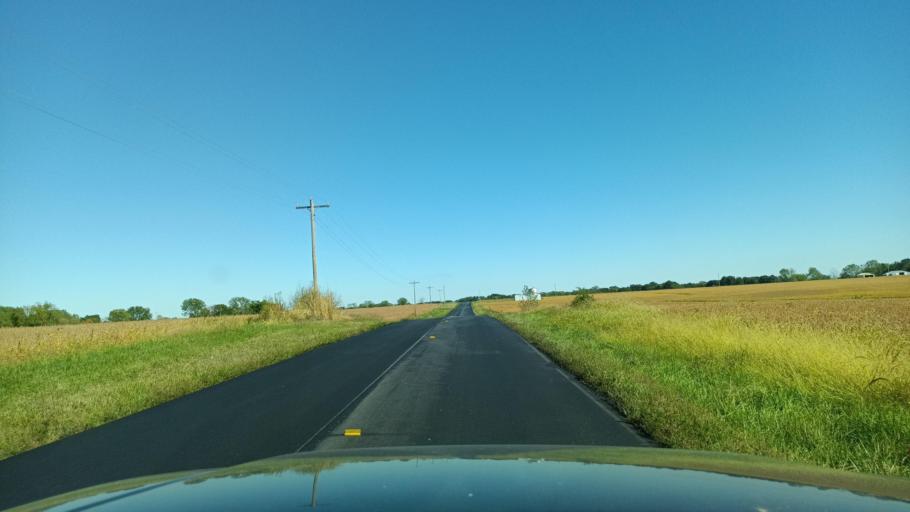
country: US
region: Missouri
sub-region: Macon County
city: La Plata
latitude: 39.9277
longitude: -92.5560
